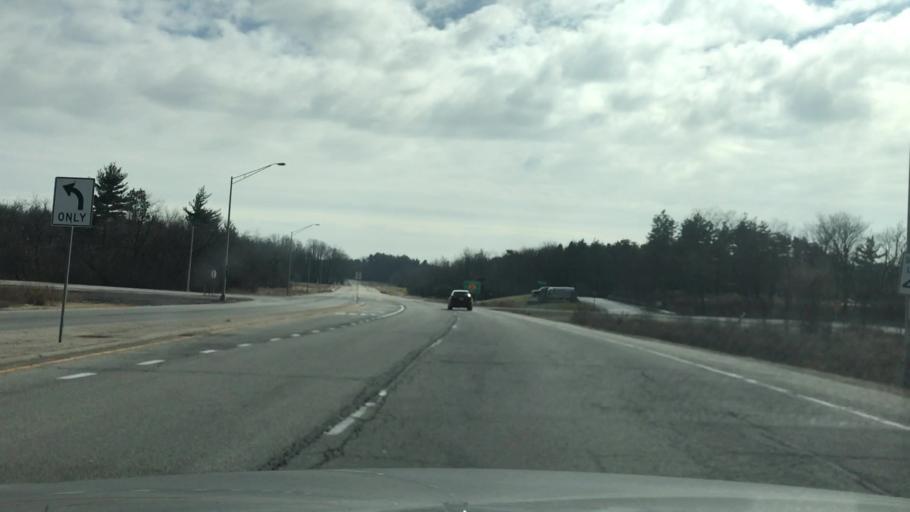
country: US
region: Illinois
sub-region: DuPage County
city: Darien
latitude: 41.7267
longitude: -87.9725
